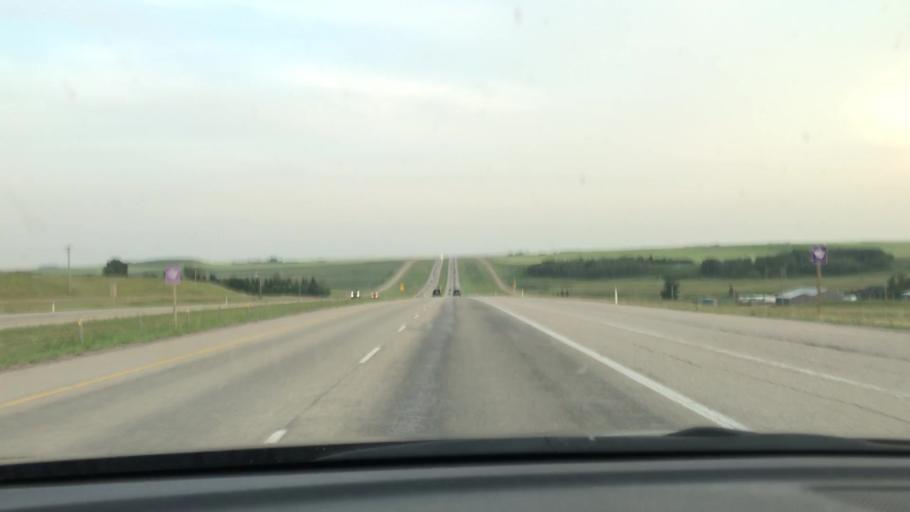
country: CA
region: Alberta
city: Carstairs
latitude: 51.5564
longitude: -114.0253
